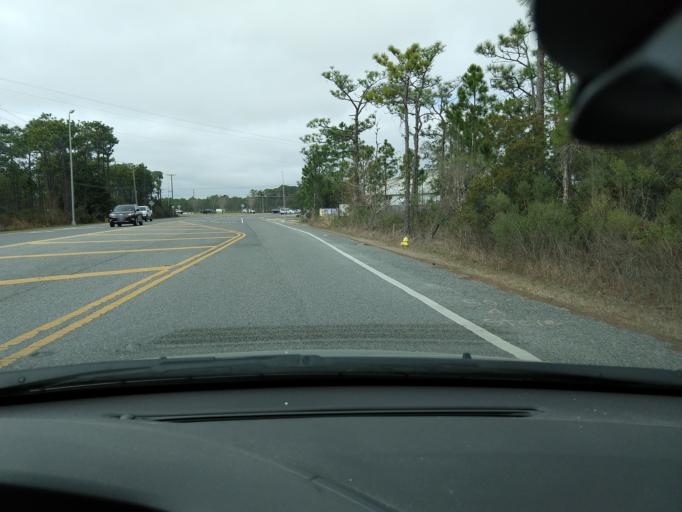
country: US
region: Florida
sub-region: Walton County
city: Miramar Beach
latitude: 30.3738
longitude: -86.2747
